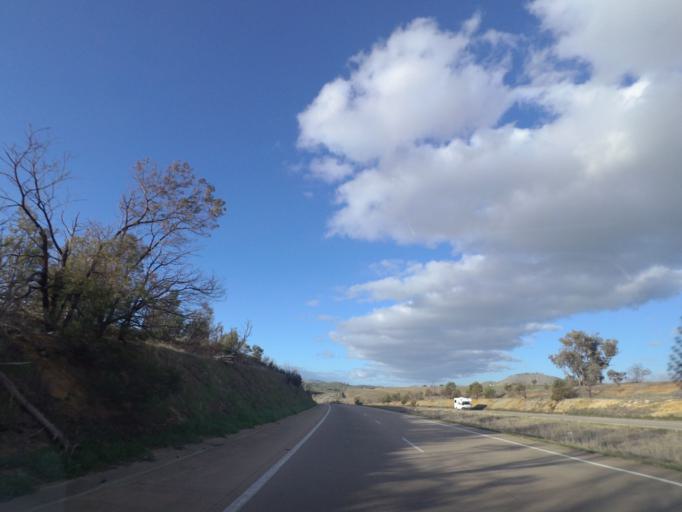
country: AU
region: New South Wales
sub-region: Gundagai
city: Gundagai
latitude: -34.8149
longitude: 148.4449
